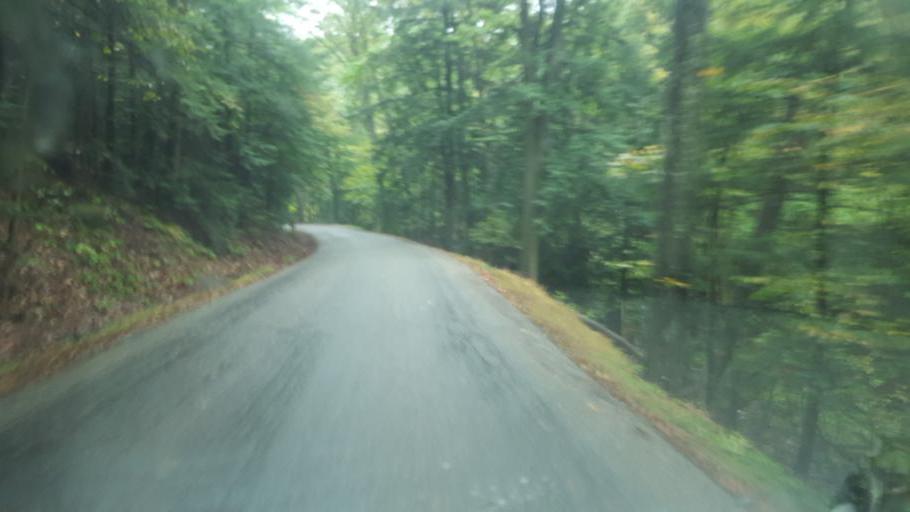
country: US
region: Ohio
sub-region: Ashland County
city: Loudonville
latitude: 40.6151
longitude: -82.3158
